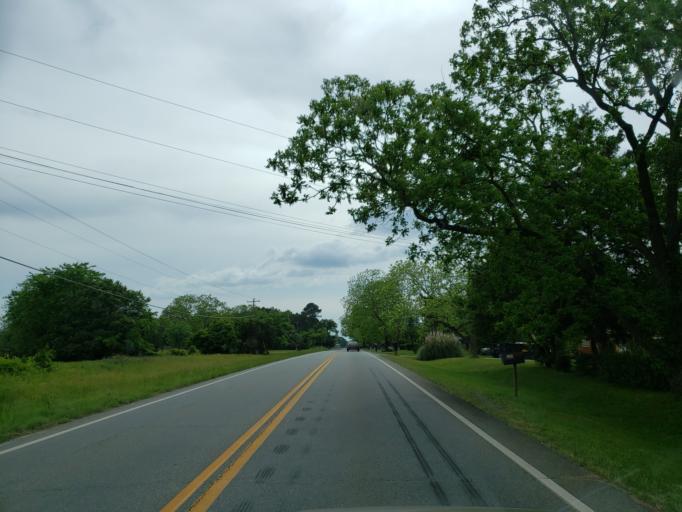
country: US
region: Georgia
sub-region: Houston County
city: Perry
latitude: 32.4450
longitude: -83.7736
